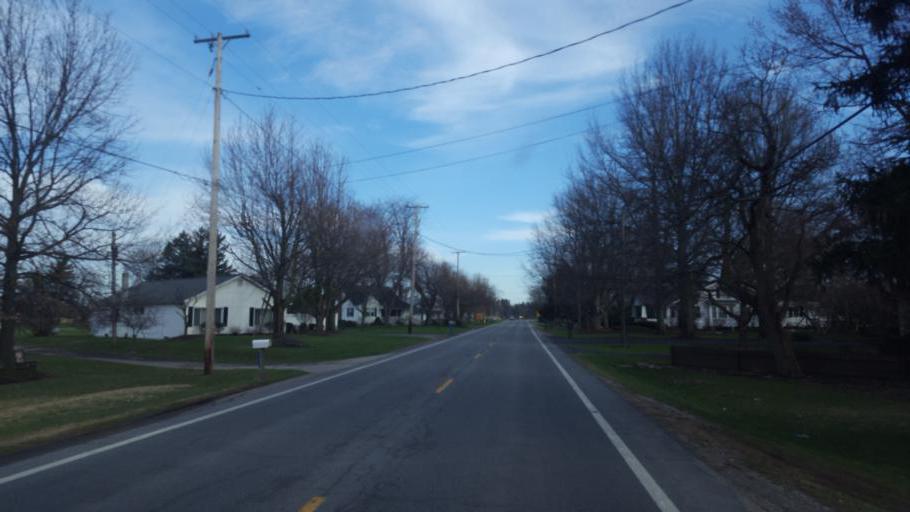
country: US
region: Ohio
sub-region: Crawford County
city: Bucyrus
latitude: 40.7855
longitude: -82.9432
